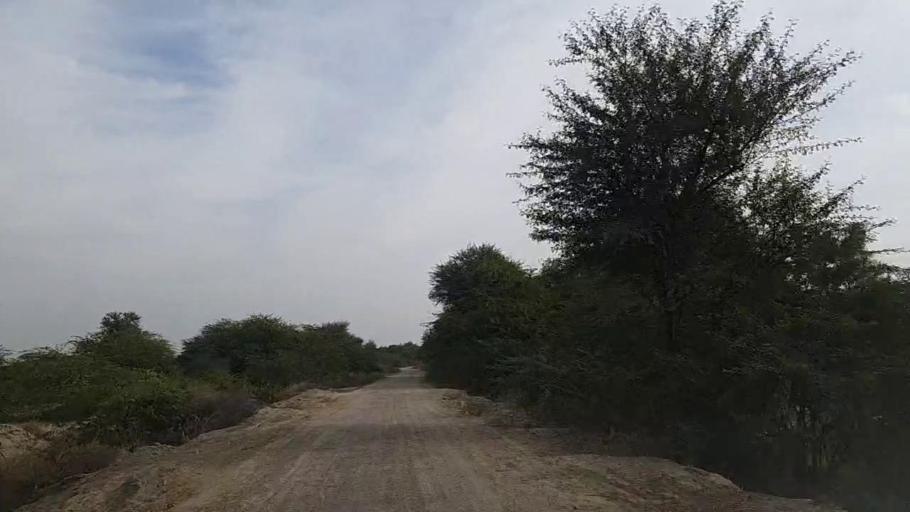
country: PK
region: Sindh
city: Jam Sahib
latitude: 26.4378
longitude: 68.6289
